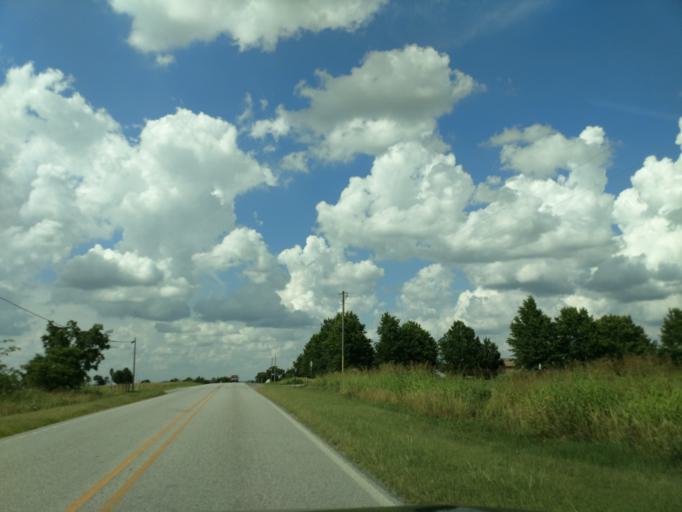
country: US
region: Arkansas
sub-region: Carroll County
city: Berryville
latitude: 36.4358
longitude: -93.5563
